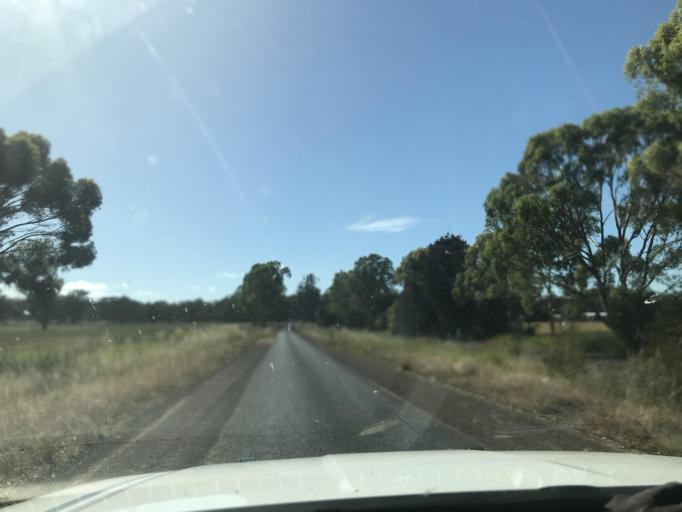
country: AU
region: Victoria
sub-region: Horsham
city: Horsham
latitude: -37.0910
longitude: 141.7683
